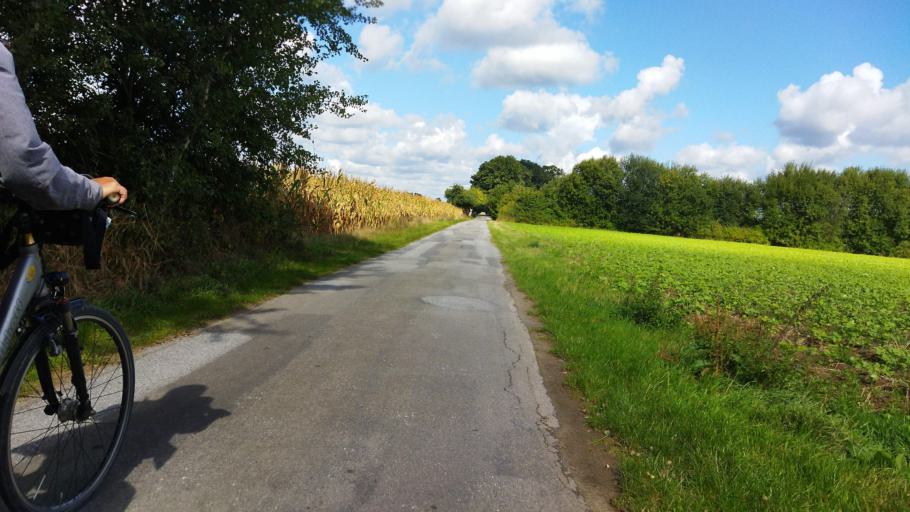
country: DE
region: Lower Saxony
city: Salzbergen
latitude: 52.3690
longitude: 7.3346
